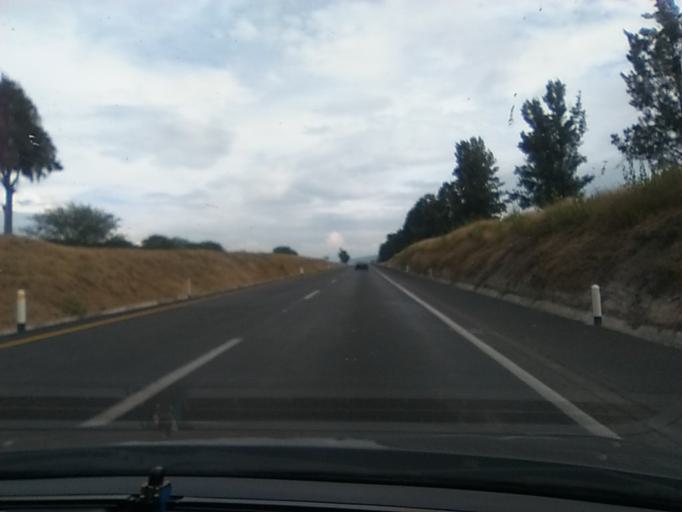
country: MX
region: Michoacan
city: Vistahermosa de Negrete
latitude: 20.2793
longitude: -102.4537
